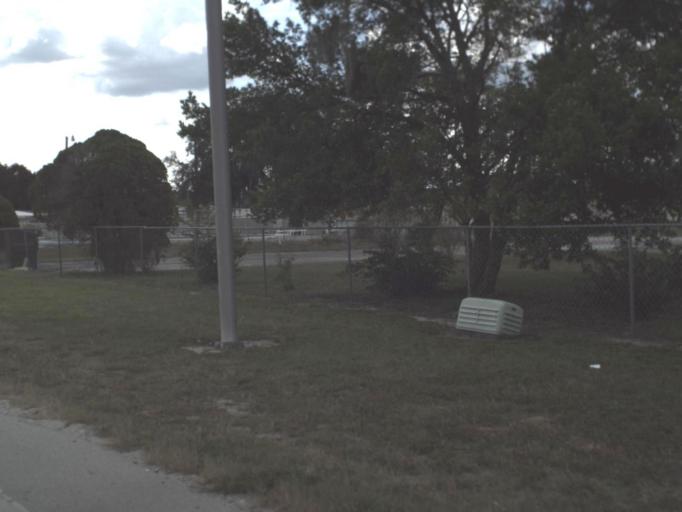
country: US
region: Florida
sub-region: Polk County
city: Winston
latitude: 28.0409
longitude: -81.9943
